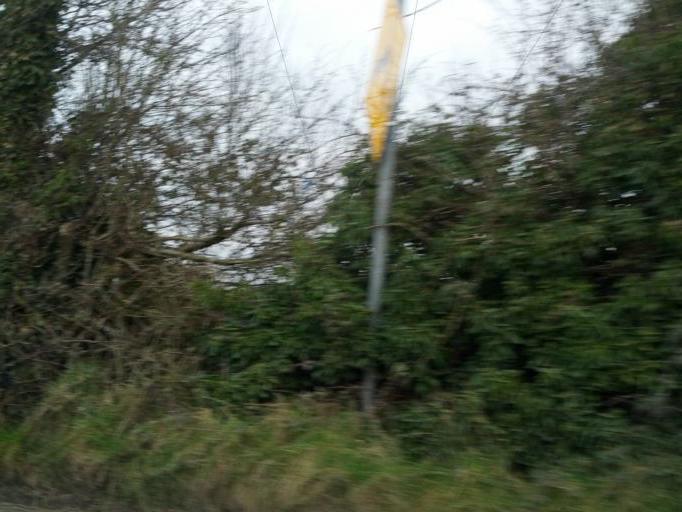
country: IE
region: Connaught
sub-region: County Galway
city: Oranmore
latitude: 53.2094
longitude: -8.8348
